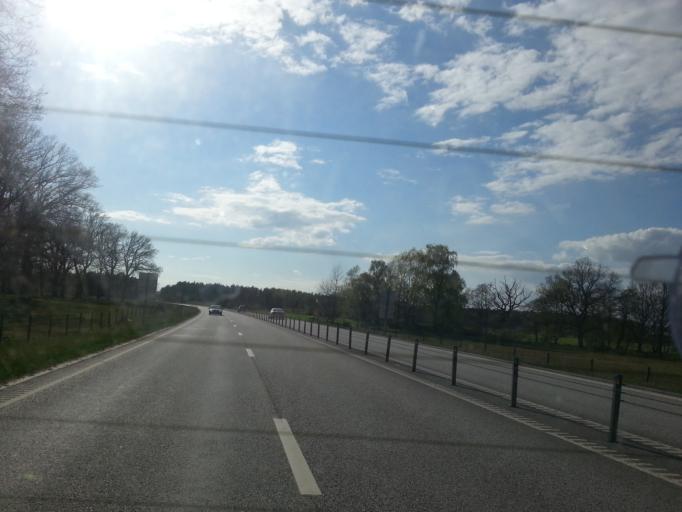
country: SE
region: Skane
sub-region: Lunds Kommun
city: Veberod
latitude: 55.6412
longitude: 13.5326
